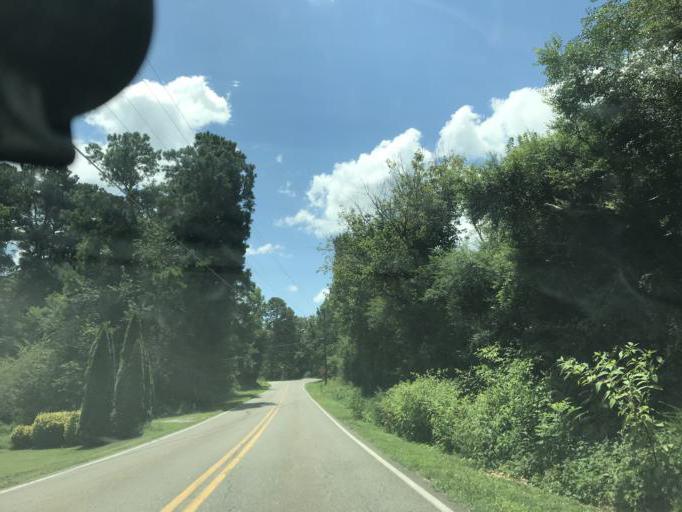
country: US
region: Georgia
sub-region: Fulton County
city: Milton
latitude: 34.2355
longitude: -84.2588
